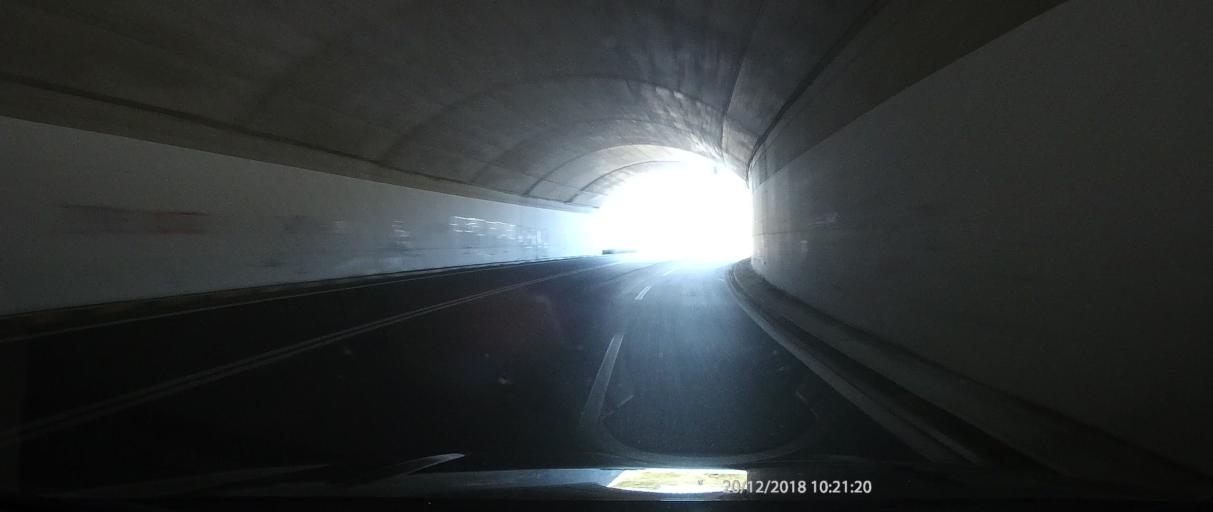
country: GR
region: Peloponnese
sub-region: Nomos Lakonias
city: Magoula
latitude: 37.1580
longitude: 22.4253
